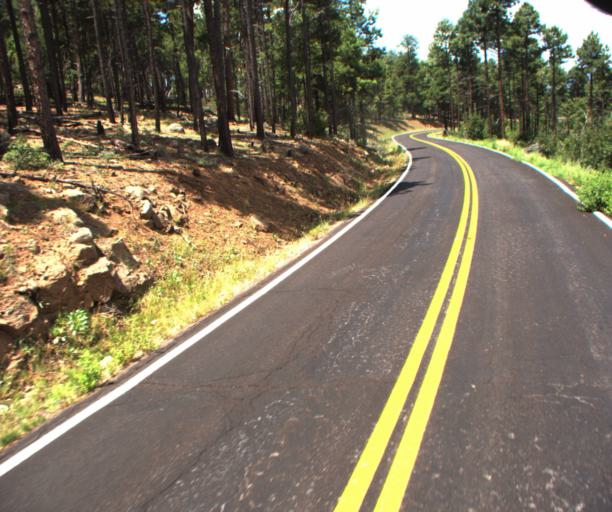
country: US
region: Arizona
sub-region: Greenlee County
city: Morenci
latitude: 33.4708
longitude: -109.3685
